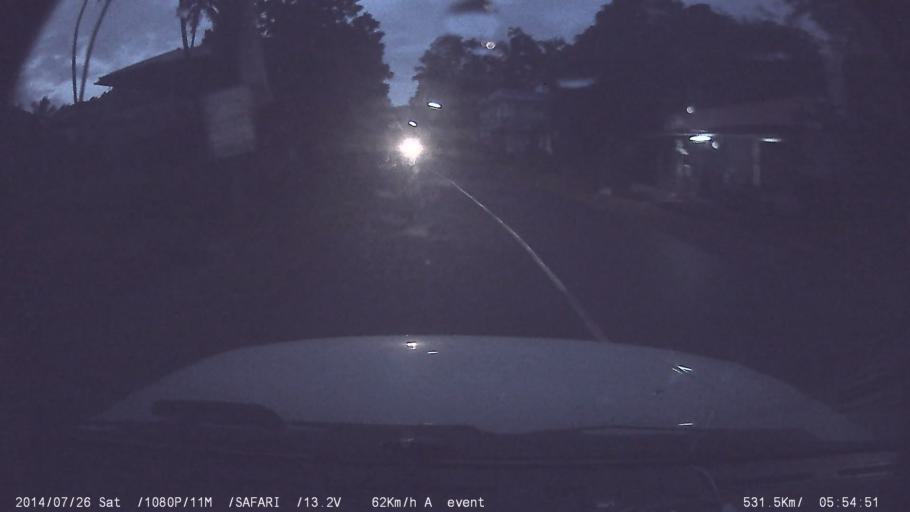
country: IN
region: Kerala
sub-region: Ernakulam
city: Muvattupuzha
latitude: 9.9449
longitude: 76.5741
